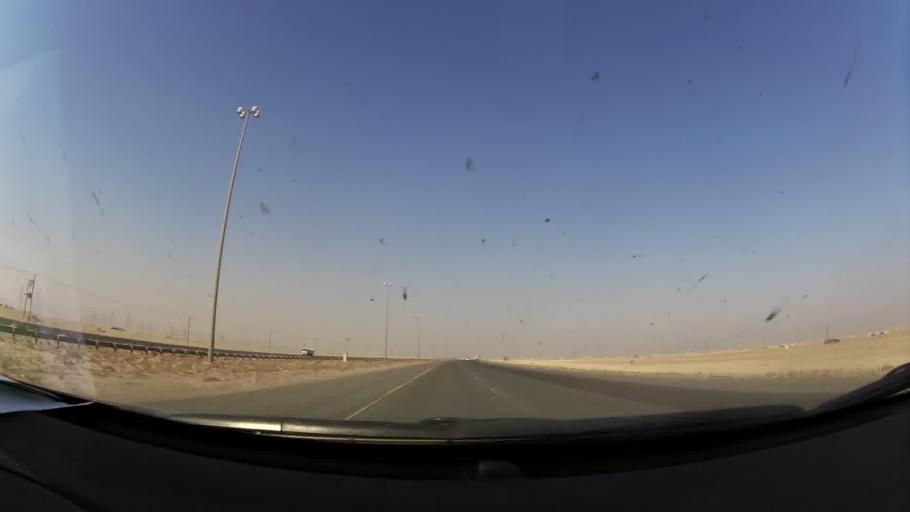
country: KW
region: Muhafazat al Jahra'
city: Al Jahra'
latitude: 29.6635
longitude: 47.6649
